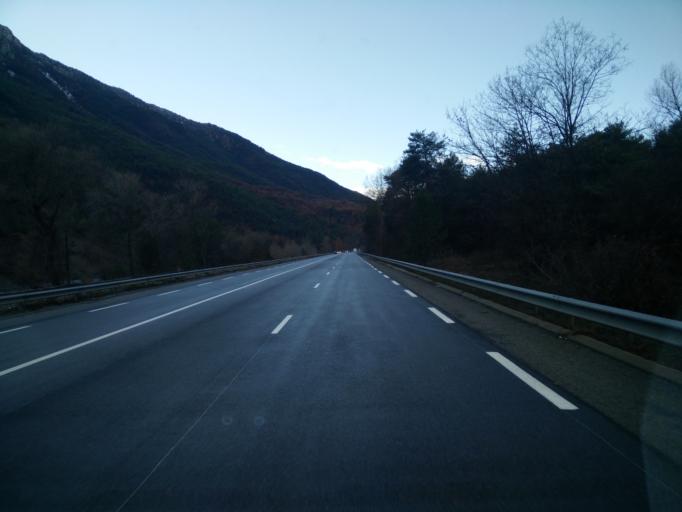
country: FR
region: Provence-Alpes-Cote d'Azur
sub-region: Departement des Alpes-Maritimes
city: Puget-Theniers
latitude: 43.9483
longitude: 6.9696
